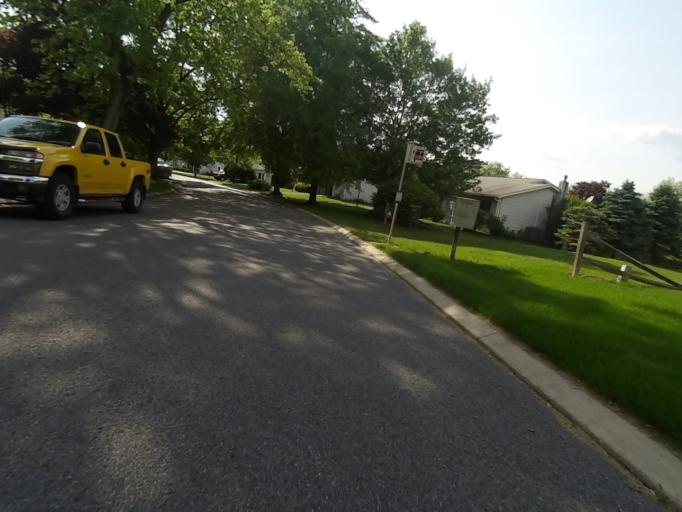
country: US
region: Pennsylvania
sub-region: Centre County
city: Houserville
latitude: 40.8312
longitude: -77.8263
